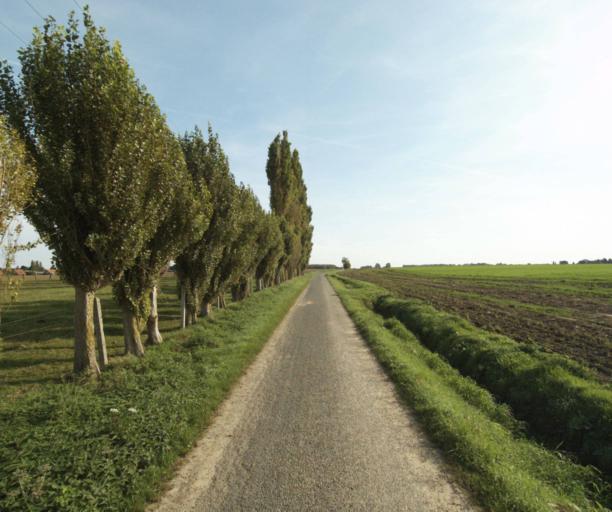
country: FR
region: Nord-Pas-de-Calais
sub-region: Departement du Nord
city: Fournes-en-Weppes
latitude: 50.5898
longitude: 2.8740
